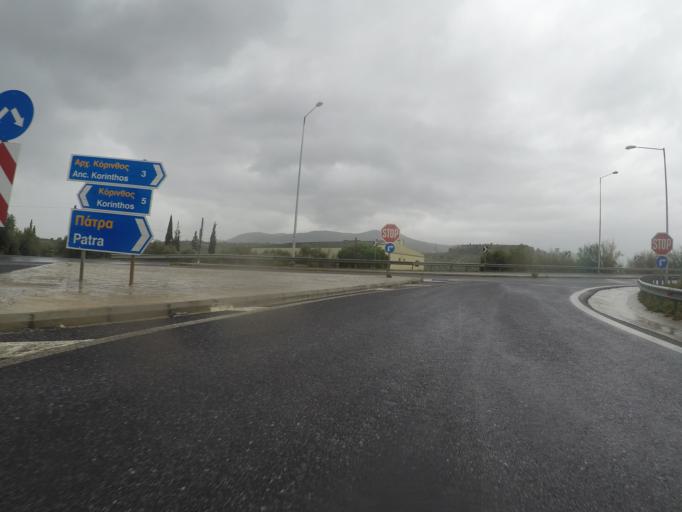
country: GR
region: Peloponnese
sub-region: Nomos Korinthias
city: Arkhaia Korinthos
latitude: 37.8972
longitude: 22.8988
